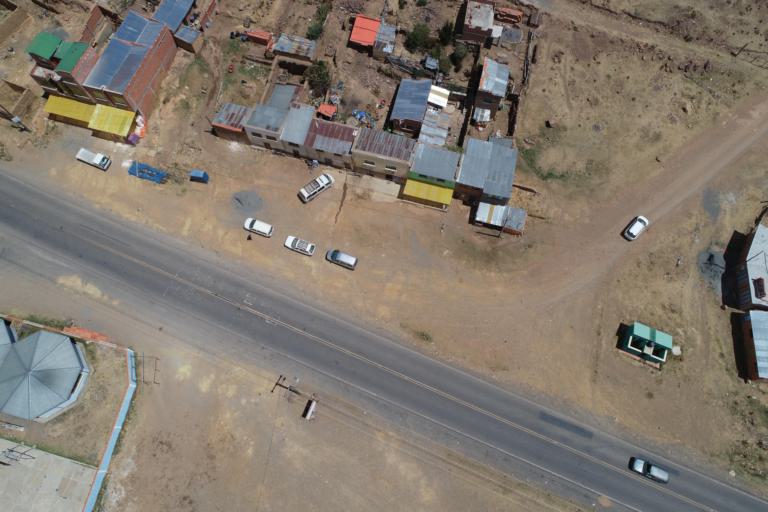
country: BO
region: La Paz
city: Achacachi
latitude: -15.9115
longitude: -68.8854
